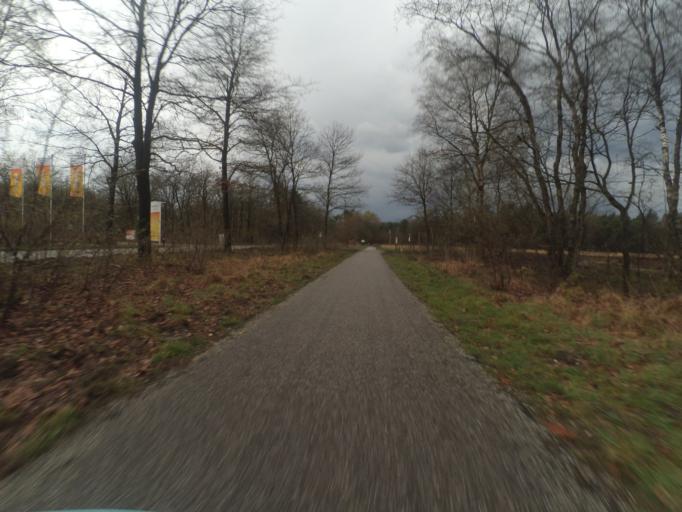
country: NL
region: Gelderland
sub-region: Gemeente Apeldoorn
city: Beekbergen
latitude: 52.1217
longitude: 5.9106
